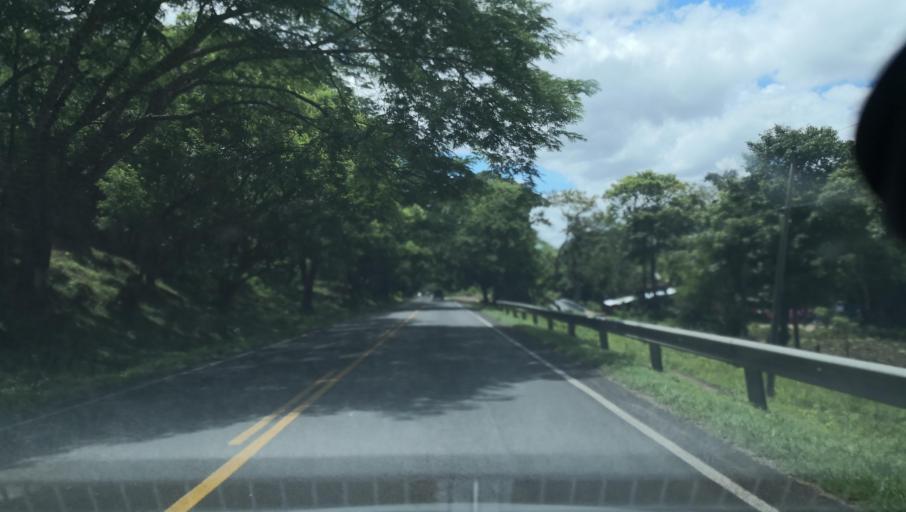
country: NI
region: Esteli
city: Condega
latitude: 13.2881
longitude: -86.3462
